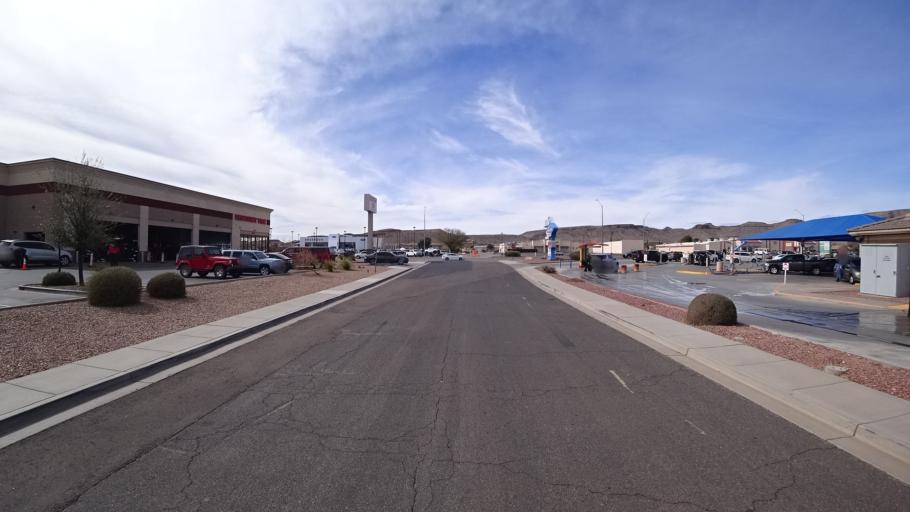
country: US
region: Arizona
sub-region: Mohave County
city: New Kingman-Butler
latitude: 35.2278
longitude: -114.0358
